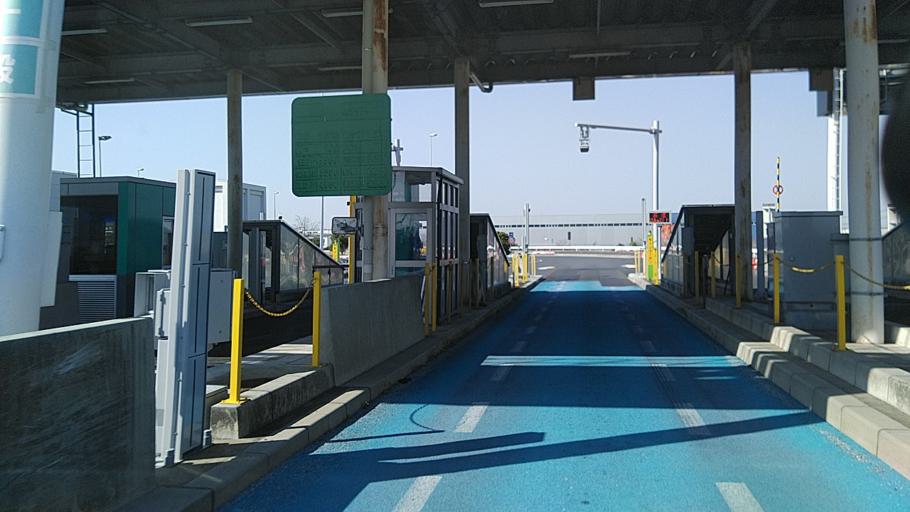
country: JP
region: Saitama
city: Kawagoe
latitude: 35.9832
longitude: 139.4656
